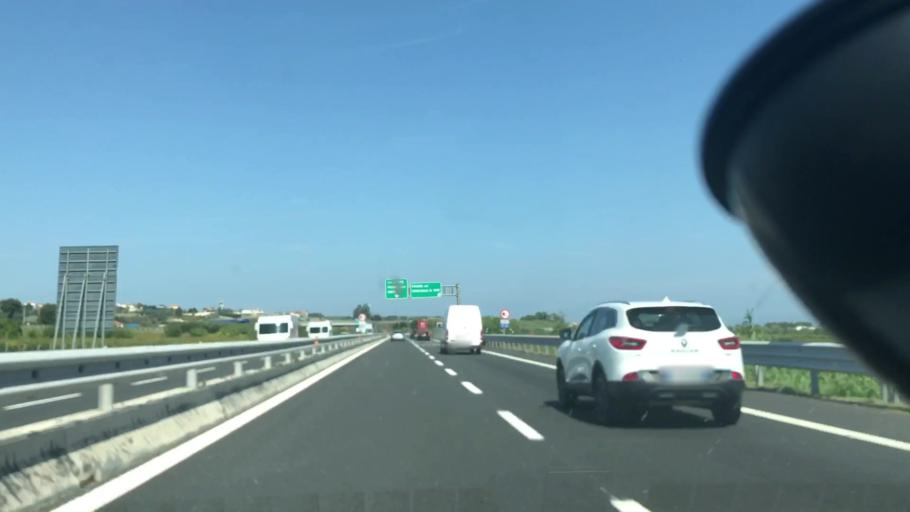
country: IT
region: Abruzzo
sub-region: Provincia di Chieti
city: Francavilla al Mare
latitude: 42.3926
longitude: 14.2888
